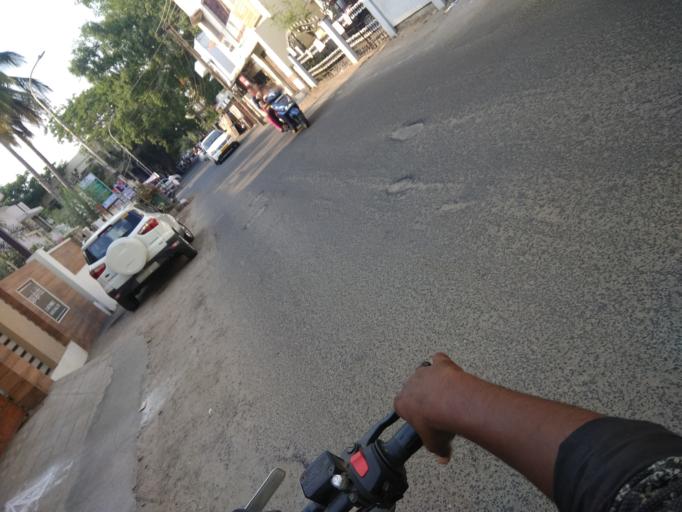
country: IN
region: Tamil Nadu
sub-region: Kancheepuram
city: Madipakkam
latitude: 12.9801
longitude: 80.1883
